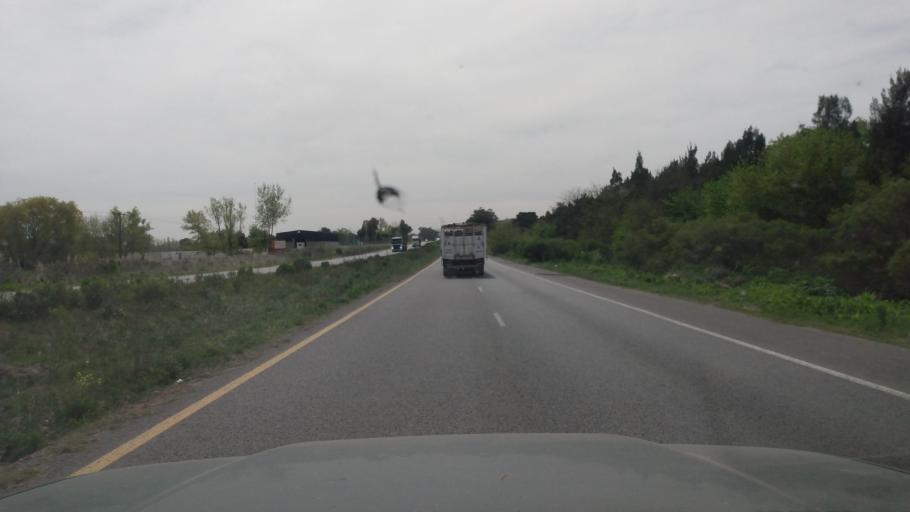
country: AR
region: Buenos Aires
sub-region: Partido de Lujan
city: Lujan
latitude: -34.4514
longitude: -59.0545
